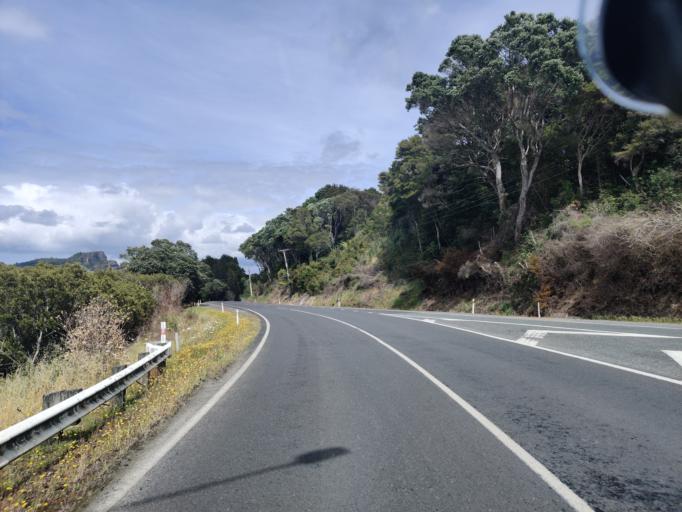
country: NZ
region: Northland
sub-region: Far North District
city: Taipa
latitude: -35.0555
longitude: 173.6996
